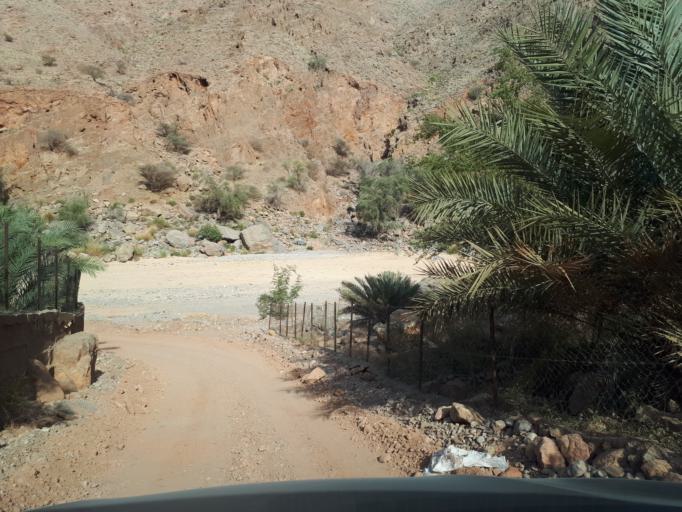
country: OM
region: Ash Sharqiyah
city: Al Qabil
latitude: 23.0667
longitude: 58.9855
